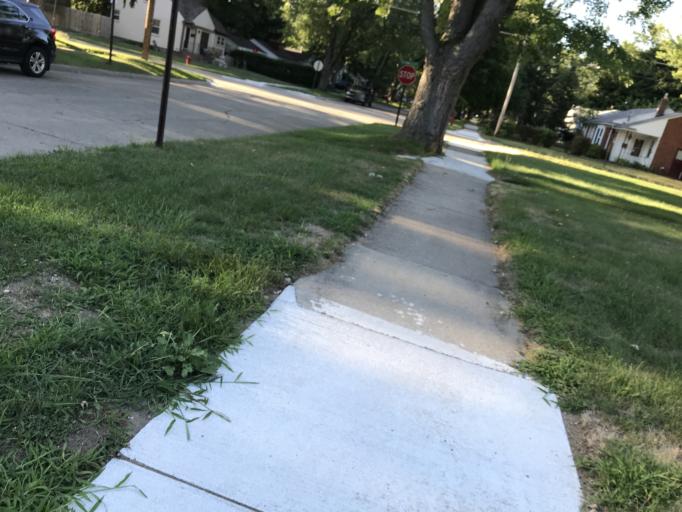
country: US
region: Michigan
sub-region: Oakland County
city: Farmington
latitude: 42.4594
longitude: -83.3528
